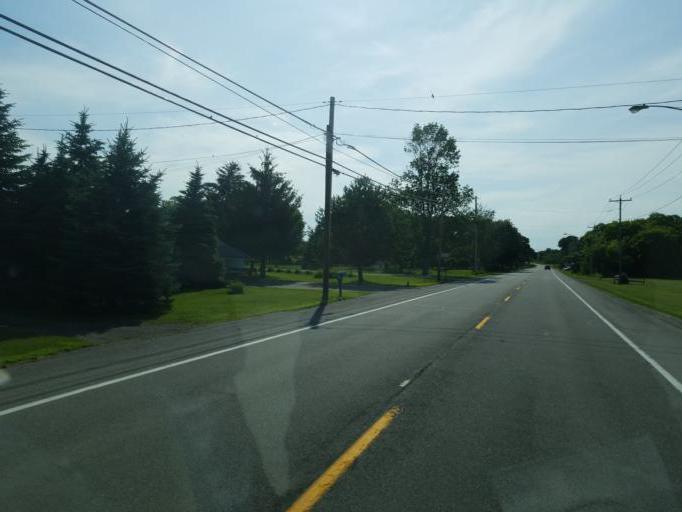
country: US
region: New York
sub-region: Livingston County
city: Caledonia
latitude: 42.9756
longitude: -77.8695
